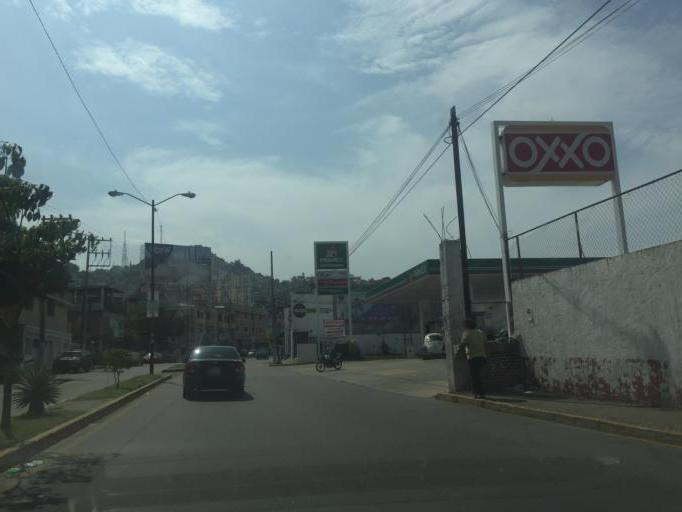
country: MX
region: Guerrero
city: Acapulco de Juarez
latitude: 16.8560
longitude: -99.9097
